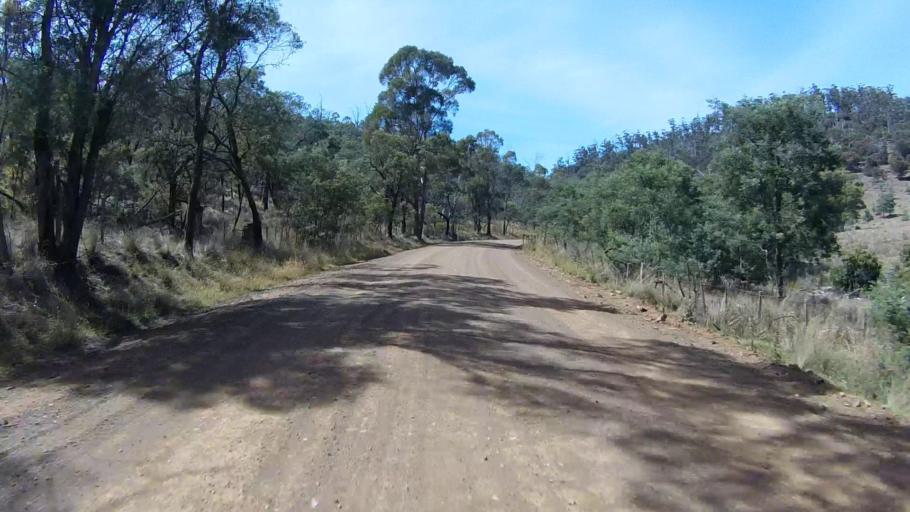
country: AU
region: Tasmania
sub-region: Sorell
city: Sorell
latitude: -42.6375
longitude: 147.7270
